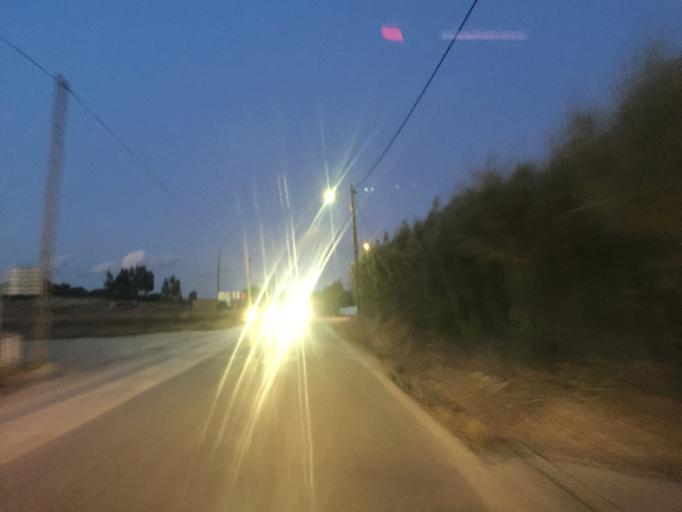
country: PT
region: Lisbon
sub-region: Lourinha
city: Lourinha
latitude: 39.2778
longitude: -9.2555
